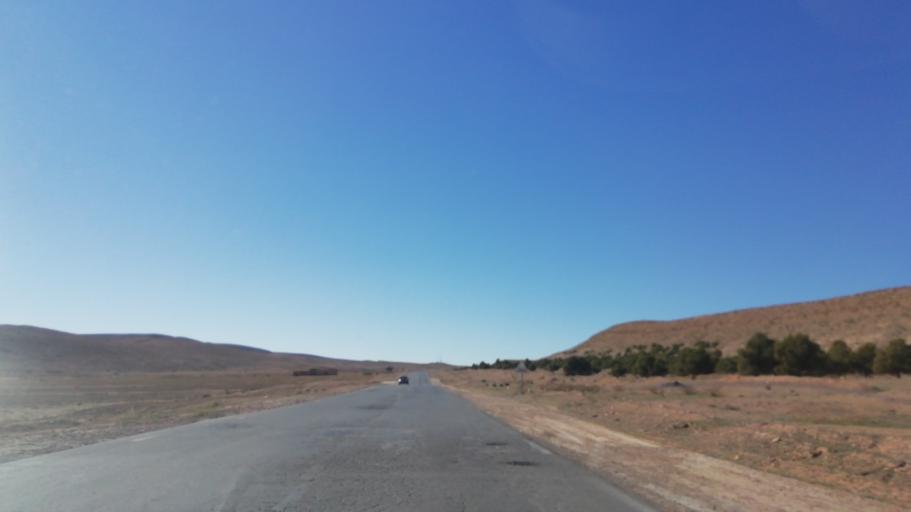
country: DZ
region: El Bayadh
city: El Bayadh
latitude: 33.6805
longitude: 1.4529
